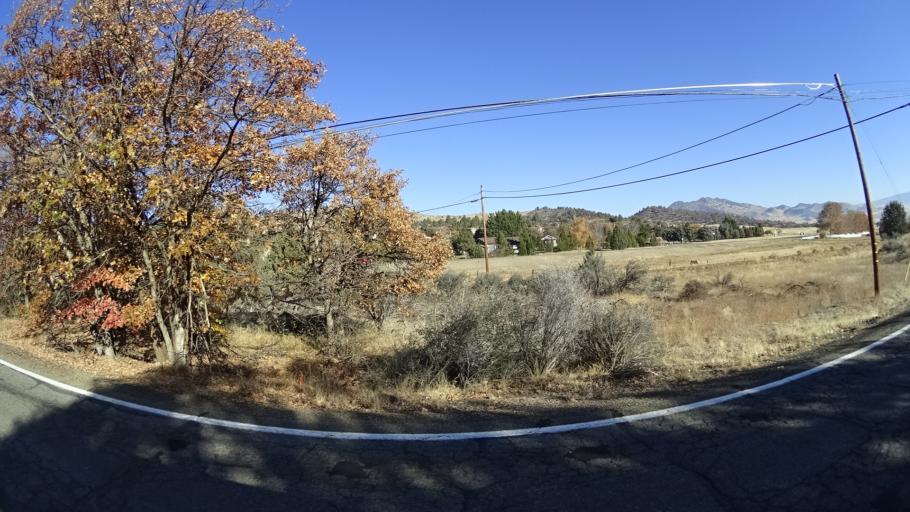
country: US
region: California
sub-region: Siskiyou County
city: Yreka
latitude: 41.7390
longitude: -122.6128
